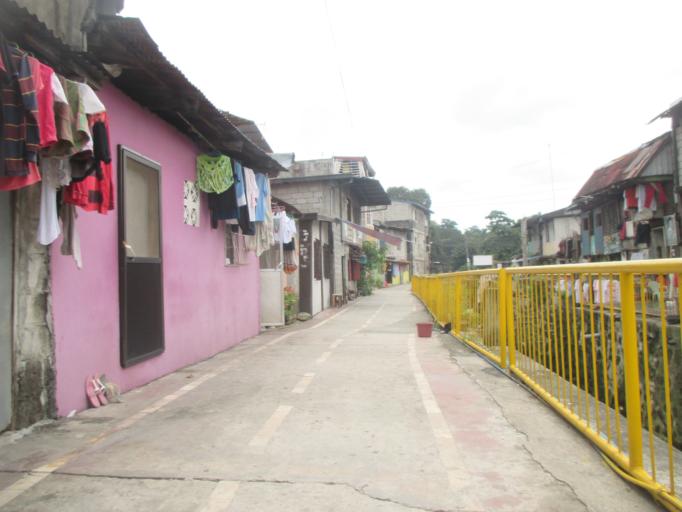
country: PH
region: Calabarzon
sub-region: Province of Rizal
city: Antipolo
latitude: 14.6522
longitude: 121.1129
